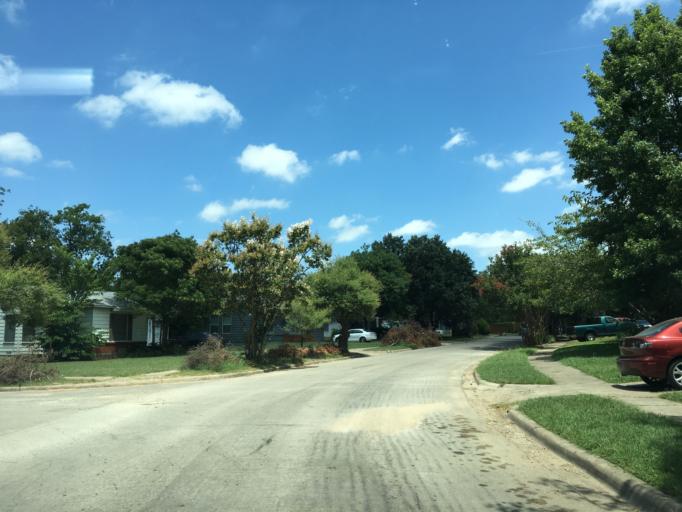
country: US
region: Texas
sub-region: Dallas County
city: Garland
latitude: 32.8393
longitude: -96.6693
